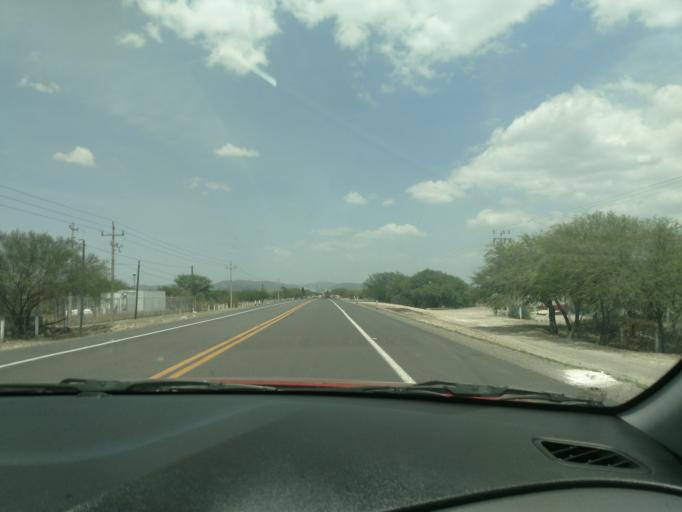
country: MX
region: San Luis Potosi
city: Rio Verde
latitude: 21.9175
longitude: -99.9485
